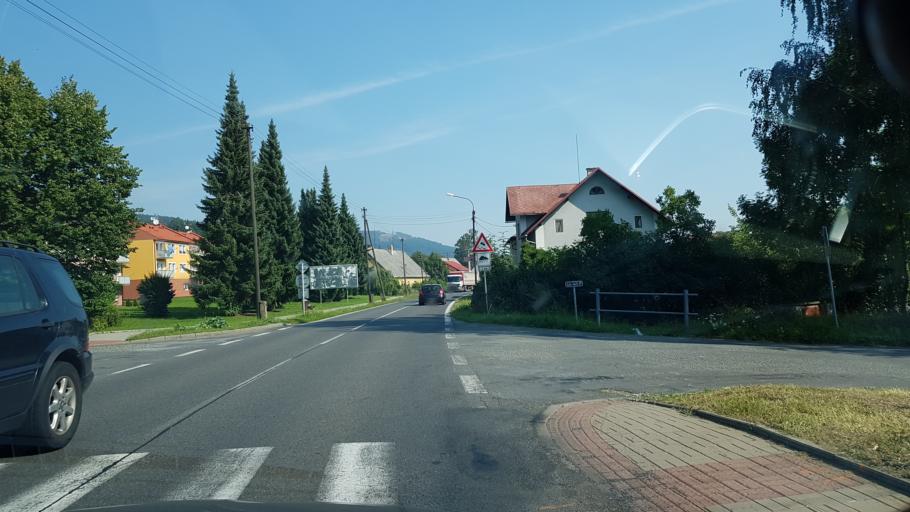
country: CZ
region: Olomoucky
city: Ceska Ves
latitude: 50.2473
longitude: 17.2137
